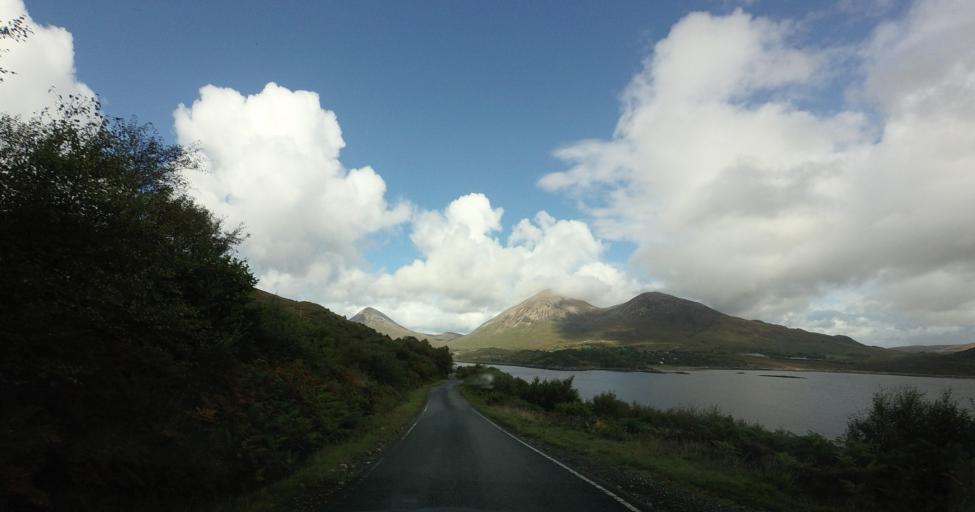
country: GB
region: Scotland
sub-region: Highland
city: Portree
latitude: 57.1961
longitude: -6.0284
